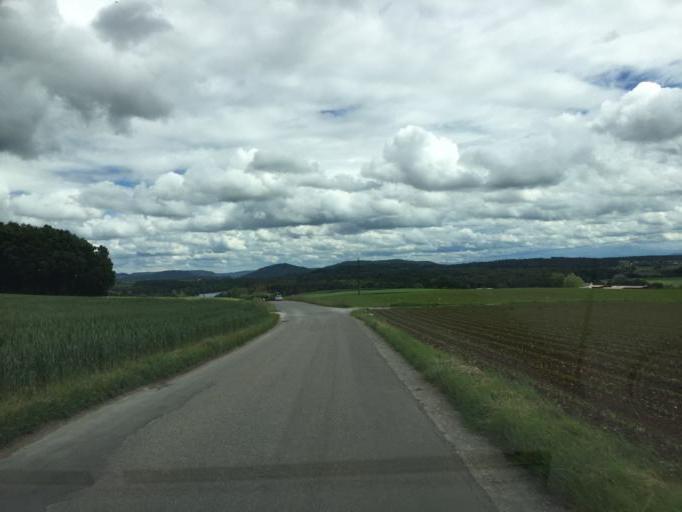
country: DE
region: Baden-Wuerttemberg
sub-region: Freiburg Region
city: Busingen
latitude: 47.6977
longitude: 8.6734
